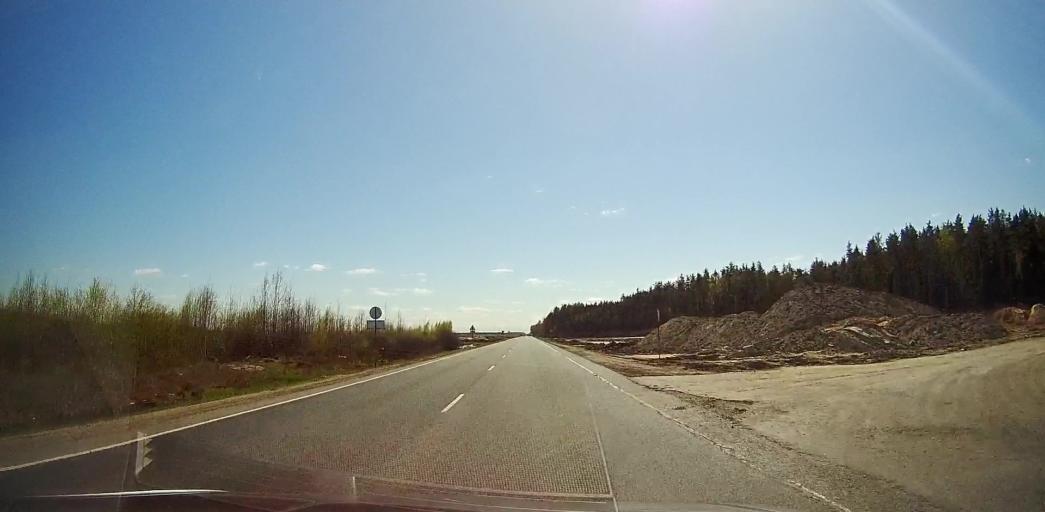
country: RU
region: Moskovskaya
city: Gzhel'
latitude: 55.5963
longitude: 38.3804
